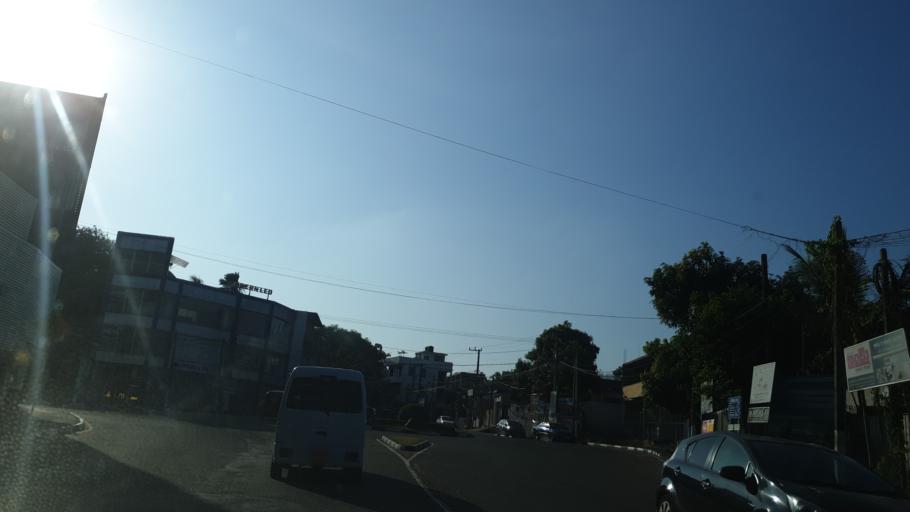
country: LK
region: Western
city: Galkissa
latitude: 6.8538
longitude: 79.8855
